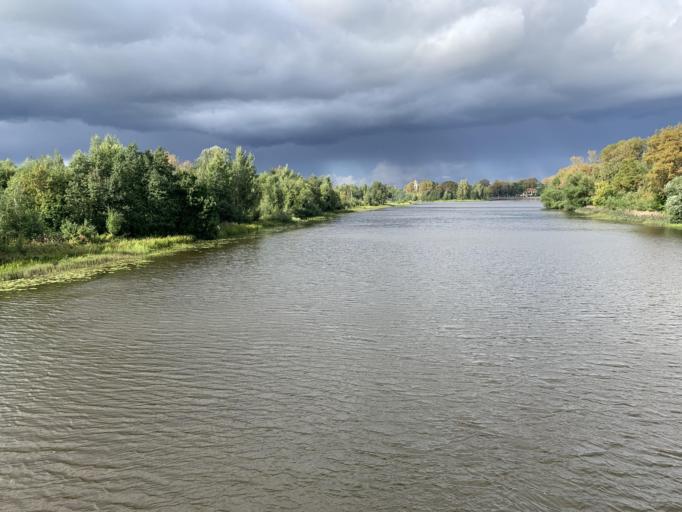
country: RU
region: Tverskaya
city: Vyshniy Volochek
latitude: 57.5745
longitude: 34.5539
